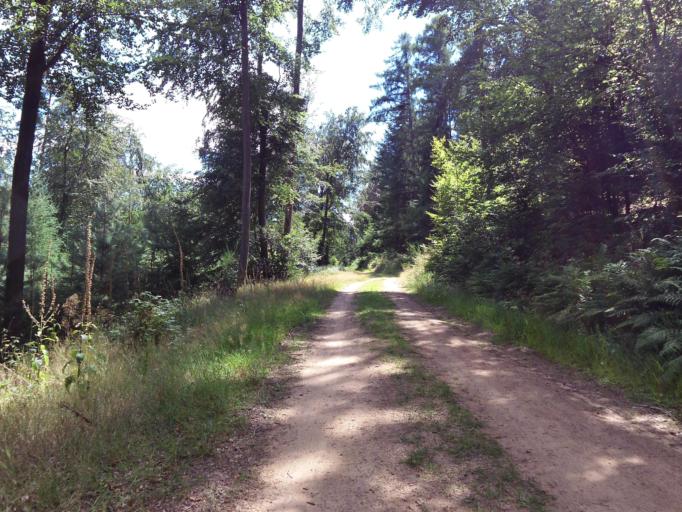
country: DE
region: Rheinland-Pfalz
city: Altleiningen
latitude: 49.4666
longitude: 8.0661
